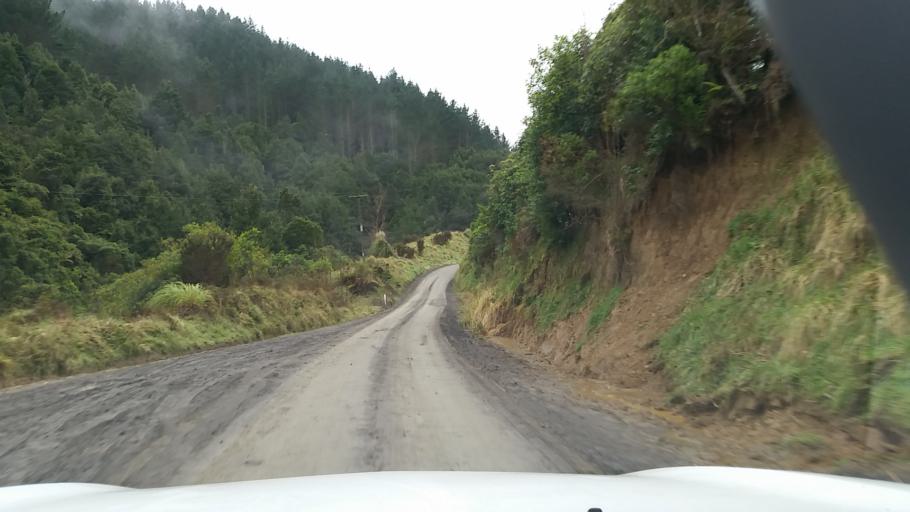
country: NZ
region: Taranaki
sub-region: South Taranaki District
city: Hawera
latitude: -39.5237
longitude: 174.4128
